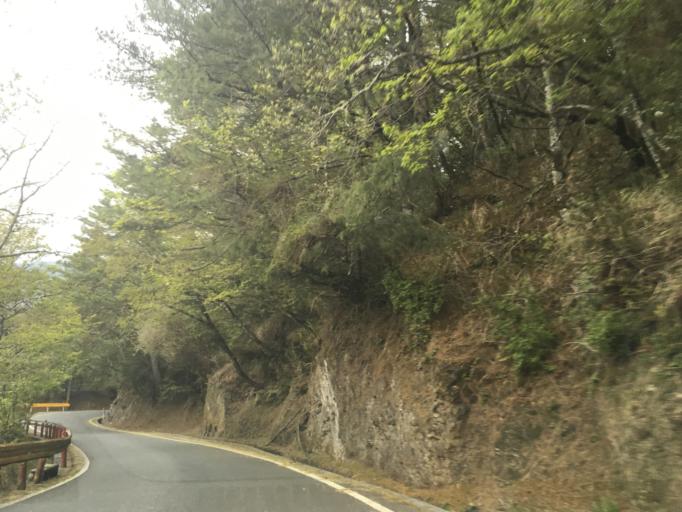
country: TW
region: Taiwan
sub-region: Hualien
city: Hualian
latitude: 24.1798
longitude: 121.3166
